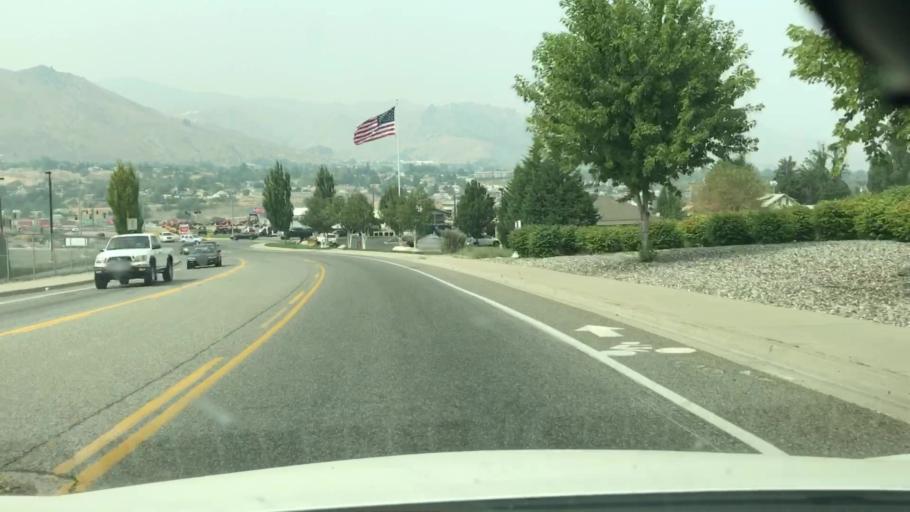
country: US
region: Washington
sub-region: Chelan County
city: South Wenatchee
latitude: 47.4005
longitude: -120.2840
